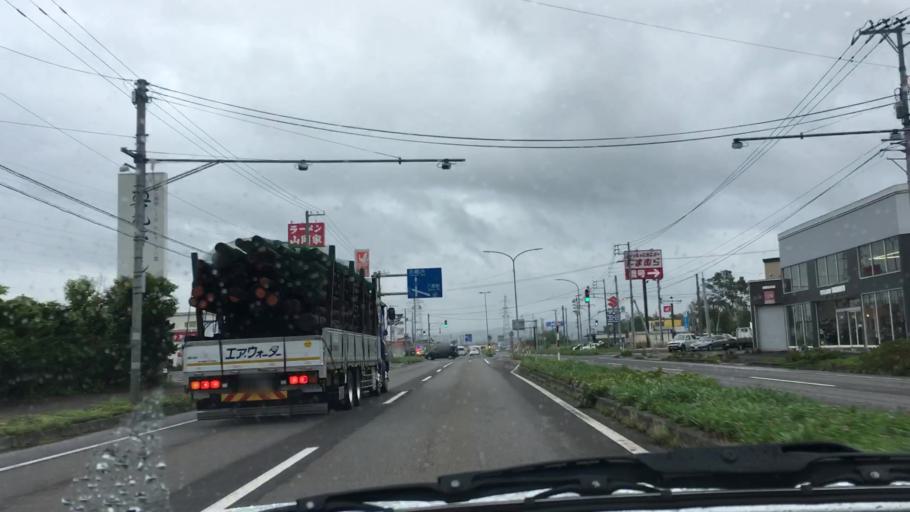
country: JP
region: Hokkaido
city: Nanae
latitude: 42.2573
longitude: 140.2795
